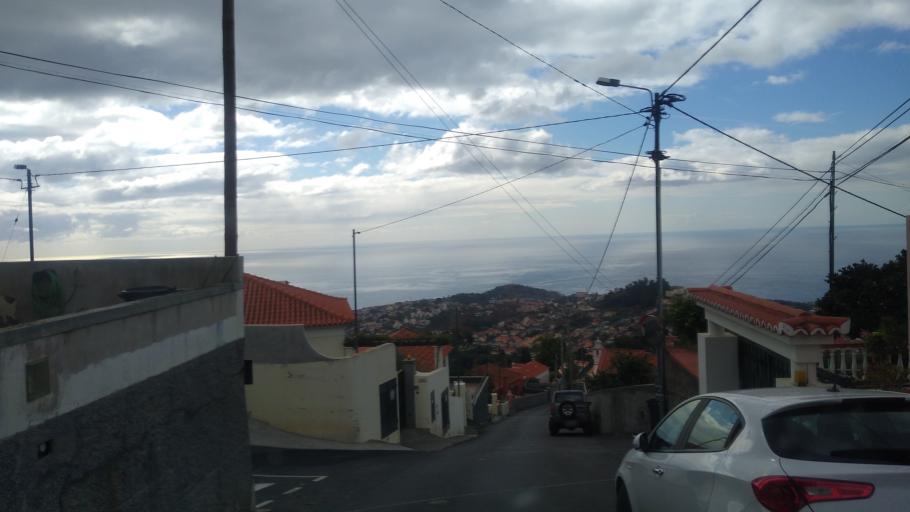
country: PT
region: Madeira
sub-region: Camara de Lobos
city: Curral das Freiras
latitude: 32.6800
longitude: -16.9464
